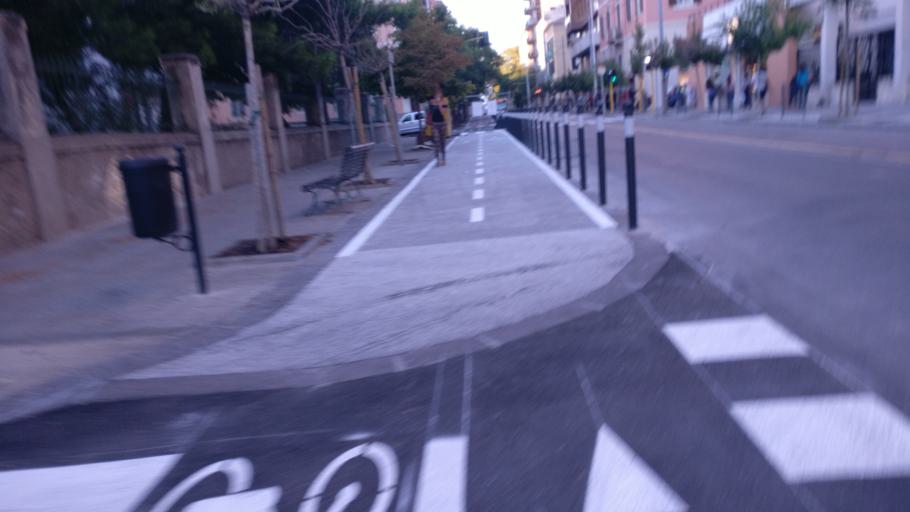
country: IT
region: Sardinia
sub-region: Provincia di Sassari
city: Sassari
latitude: 40.7211
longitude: 8.5585
